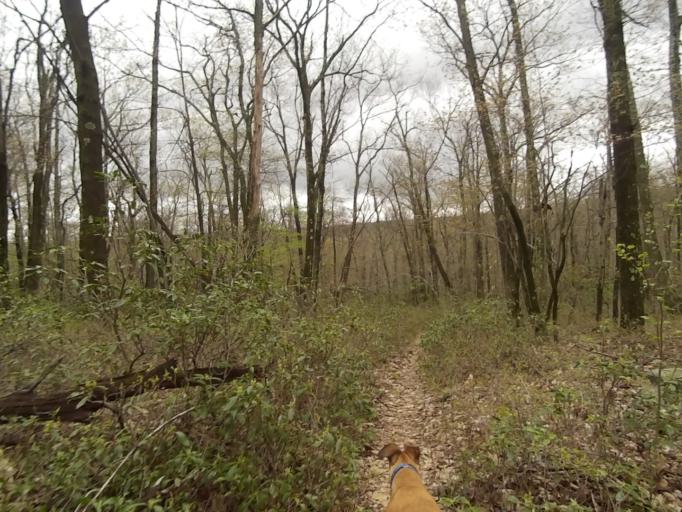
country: US
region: Pennsylvania
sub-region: Centre County
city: Boalsburg
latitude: 40.7465
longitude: -77.7504
